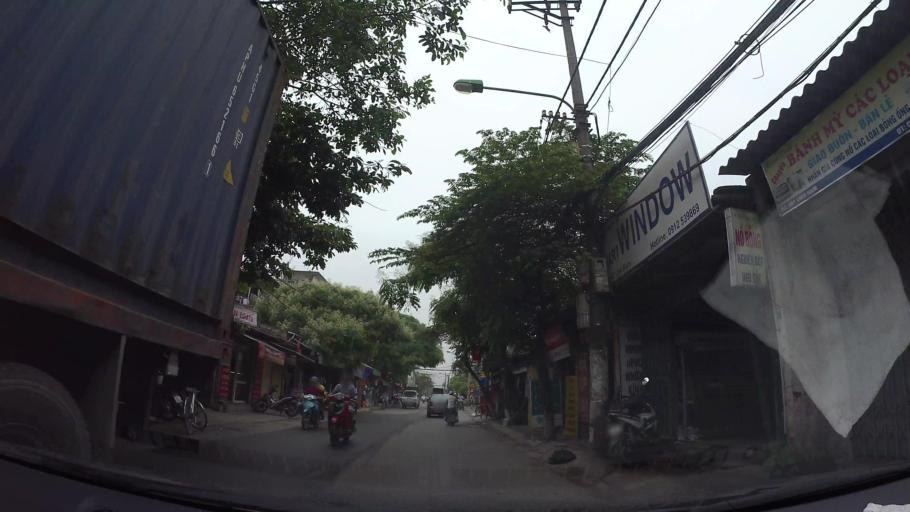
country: VN
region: Ha Noi
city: Hai BaTrung
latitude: 20.9800
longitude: 105.8871
